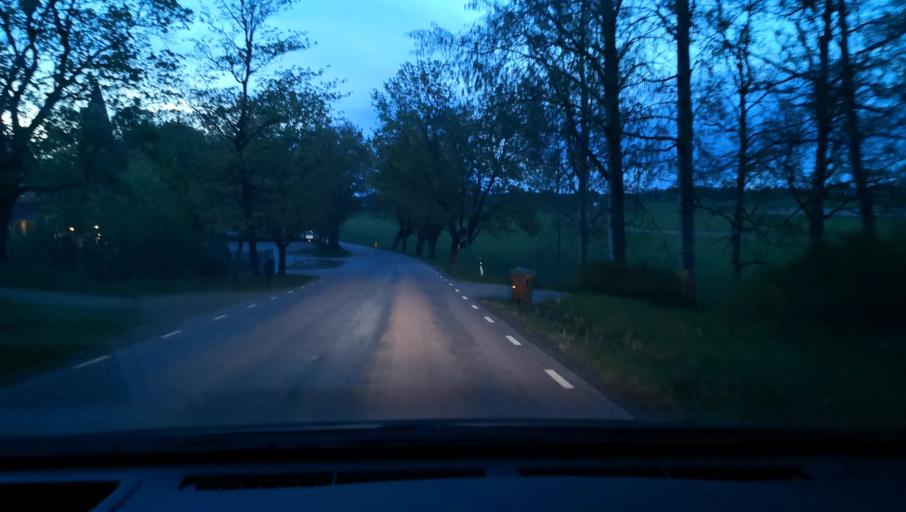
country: SE
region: OErebro
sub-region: Hallsbergs Kommun
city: Hallsberg
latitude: 59.1043
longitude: 15.0066
